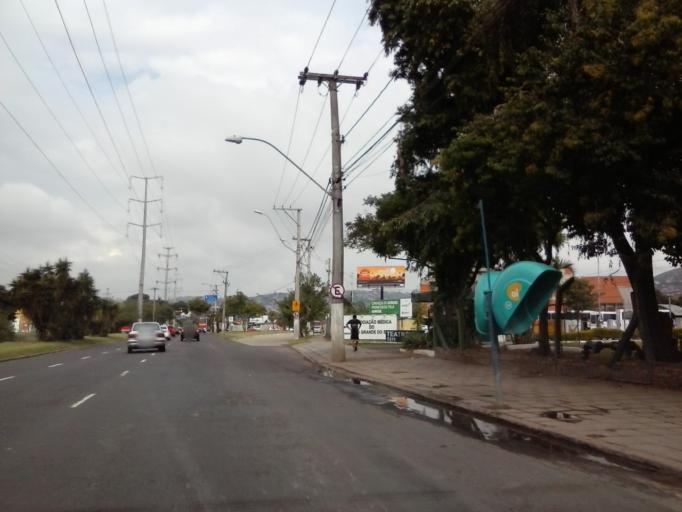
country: BR
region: Rio Grande do Sul
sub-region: Porto Alegre
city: Porto Alegre
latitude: -30.0570
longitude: -51.1866
